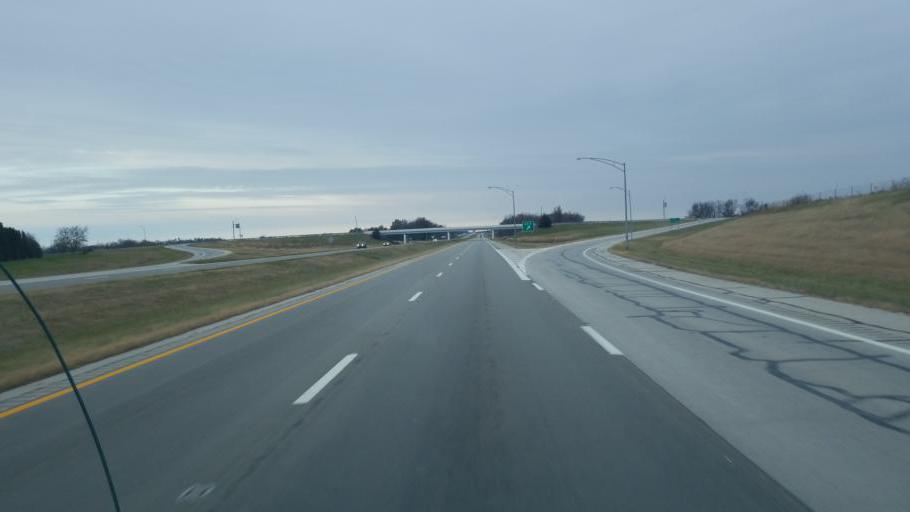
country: US
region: Ohio
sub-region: Auglaize County
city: Saint Marys
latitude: 40.5612
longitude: -84.2944
